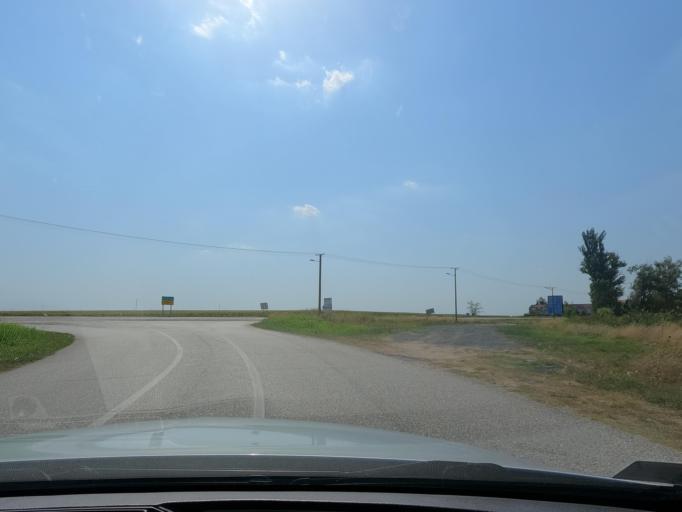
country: RS
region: Autonomna Pokrajina Vojvodina
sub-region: Severnobacki Okrug
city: Subotica
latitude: 46.0611
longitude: 19.7486
